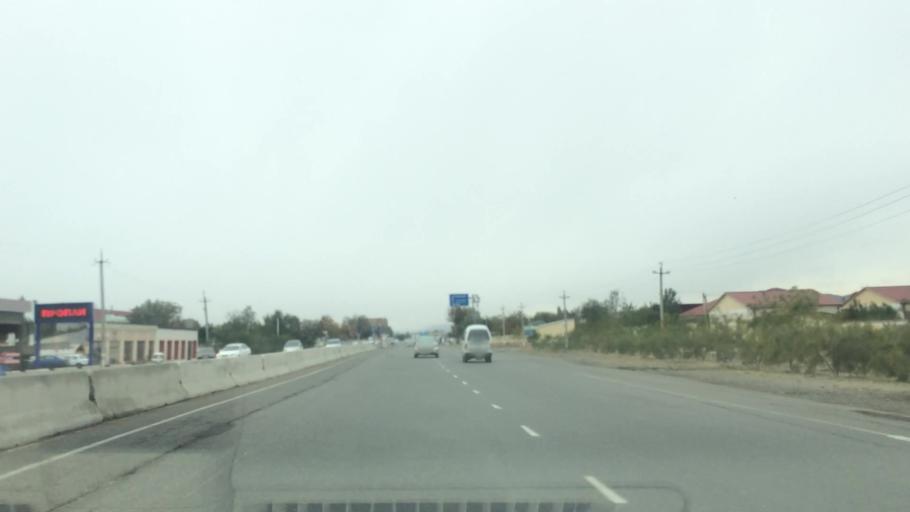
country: UZ
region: Samarqand
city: Jomboy
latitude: 39.7009
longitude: 67.0765
